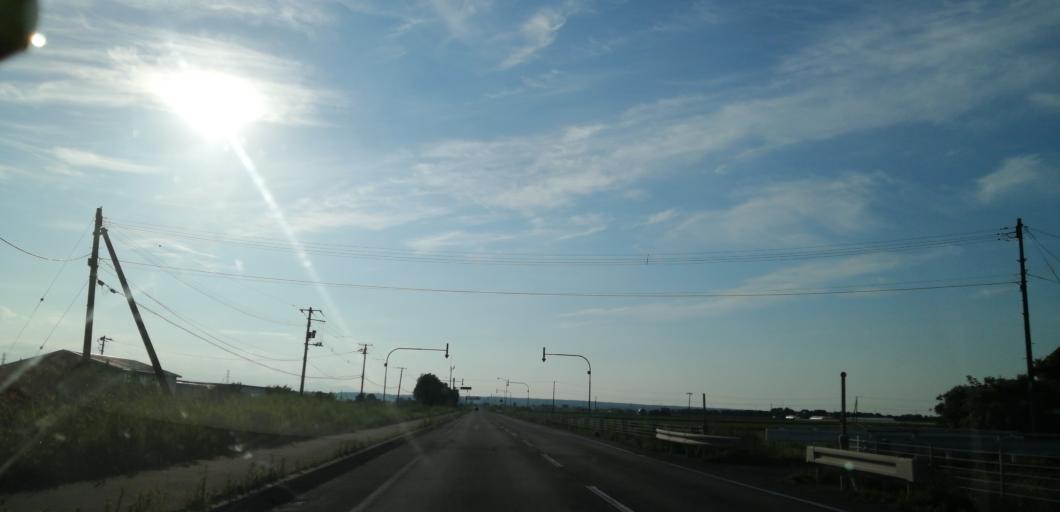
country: JP
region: Hokkaido
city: Kitahiroshima
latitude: 42.9885
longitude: 141.6120
